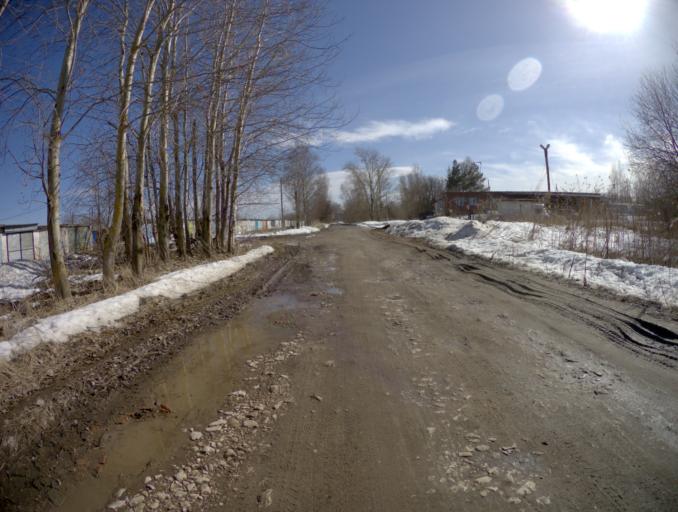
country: RU
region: Vladimir
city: Suzdal'
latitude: 56.4448
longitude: 40.4616
